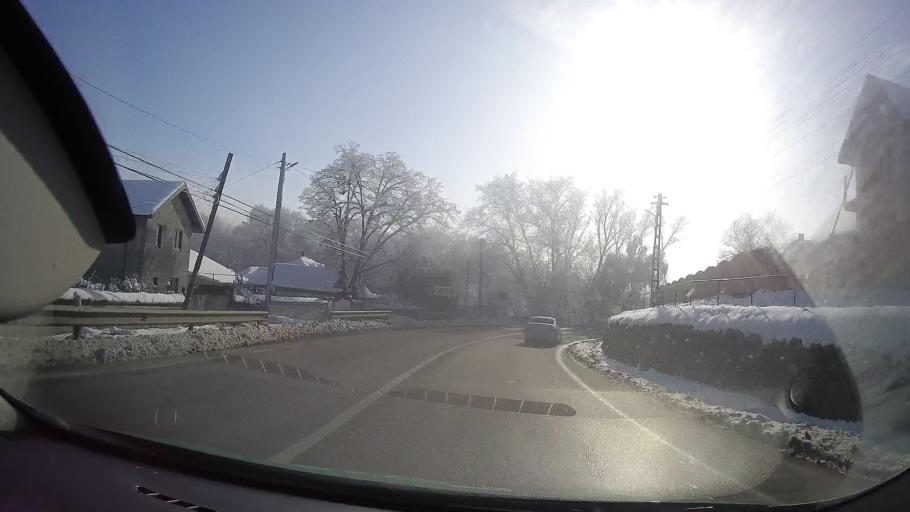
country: RO
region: Iasi
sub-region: Comuna Motca
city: Motca
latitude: 47.2363
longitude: 26.6036
